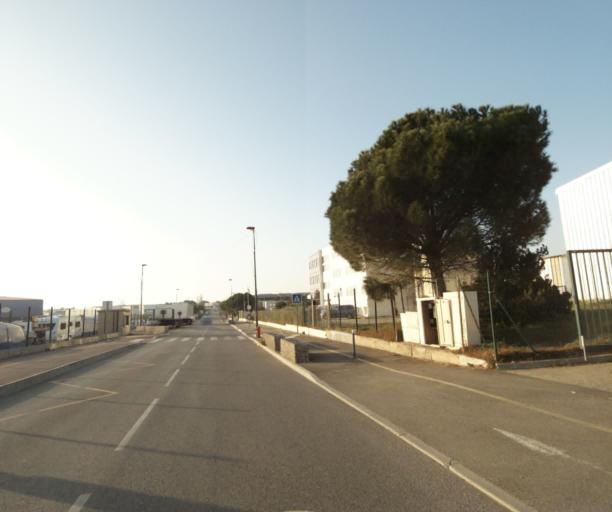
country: FR
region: Provence-Alpes-Cote d'Azur
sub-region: Departement des Bouches-du-Rhone
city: Saint-Victoret
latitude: 43.4322
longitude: 5.2477
